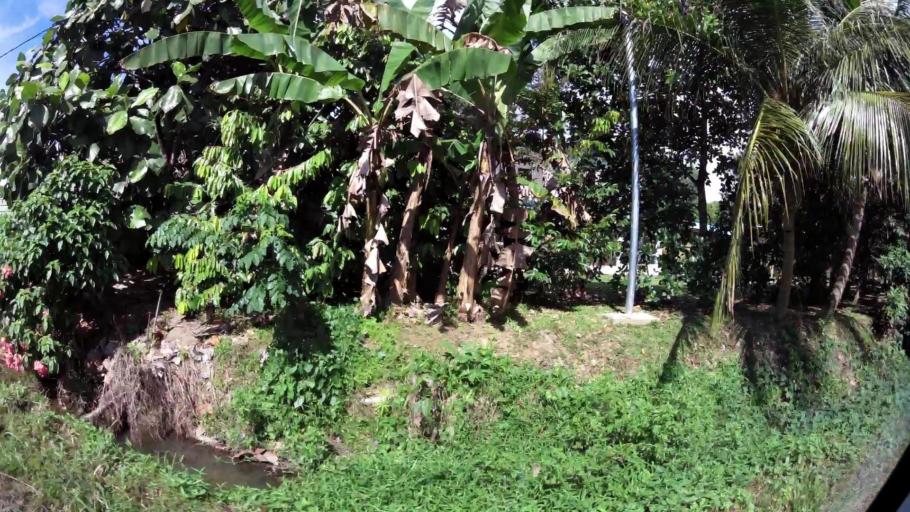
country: BN
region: Brunei and Muara
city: Bandar Seri Begawan
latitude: 5.0271
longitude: 115.0503
